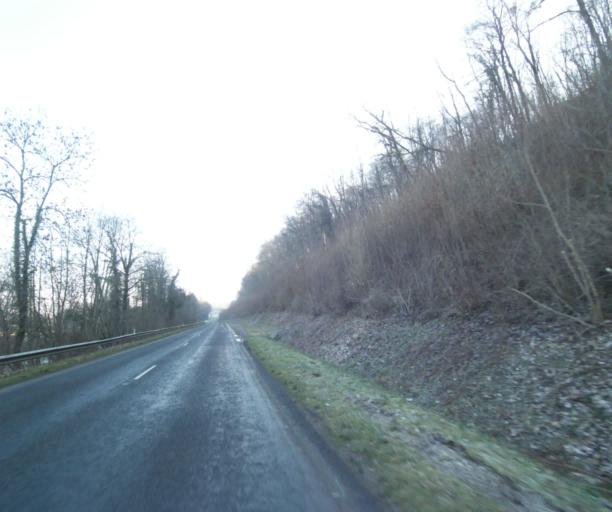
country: FR
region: Champagne-Ardenne
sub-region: Departement de la Haute-Marne
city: Bienville
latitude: 48.5541
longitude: 5.0671
